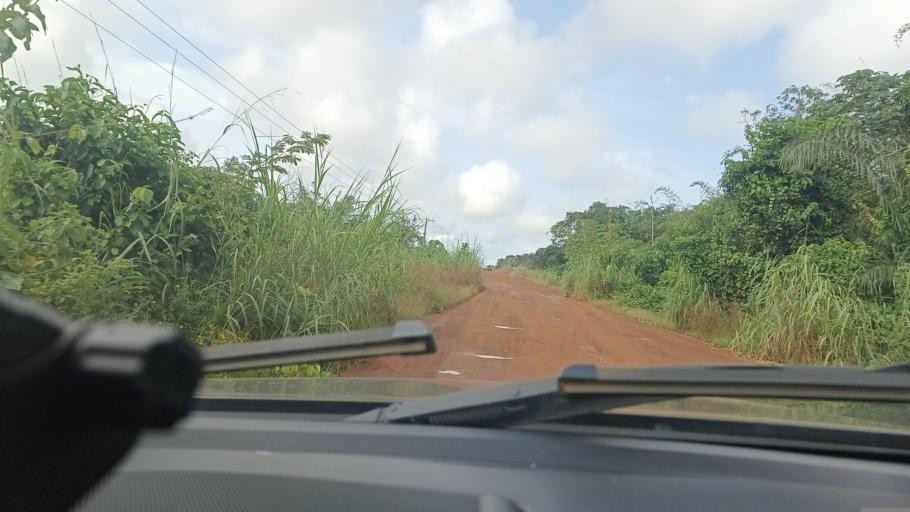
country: LR
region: Grand Cape Mount
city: Robertsport
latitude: 6.6990
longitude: -11.0968
